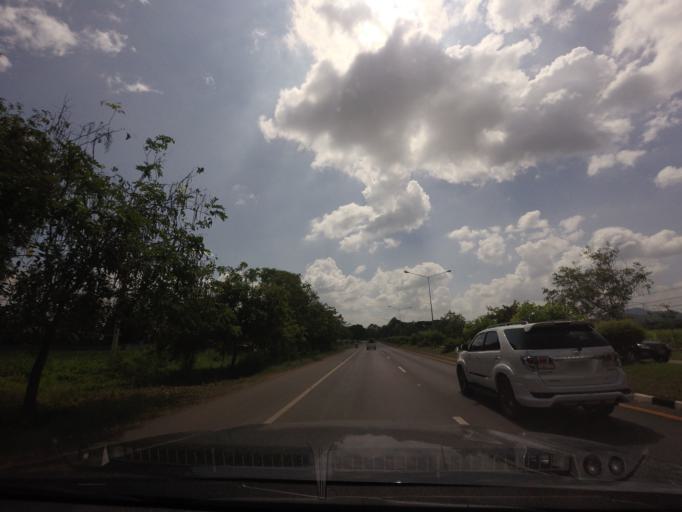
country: TH
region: Phetchabun
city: Nong Phai
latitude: 16.1203
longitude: 101.0379
